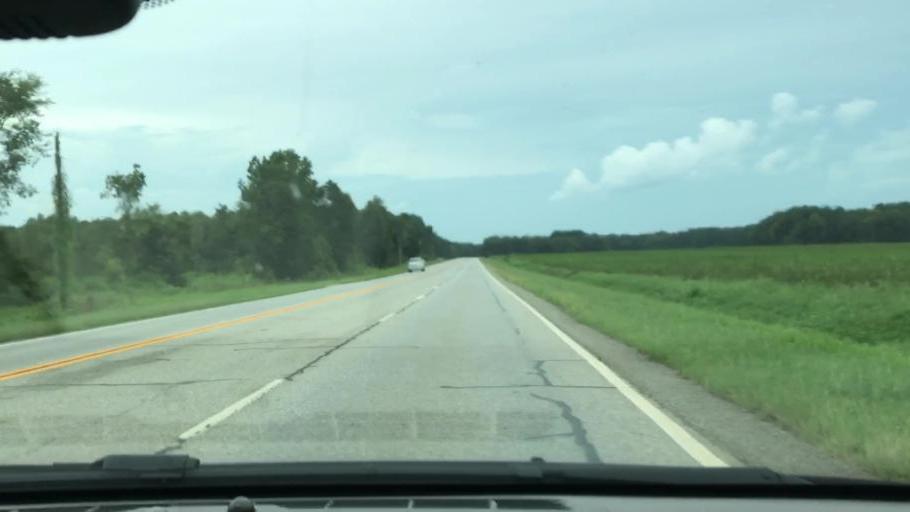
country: US
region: Georgia
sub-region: Early County
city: Blakely
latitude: 31.3398
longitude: -84.9862
